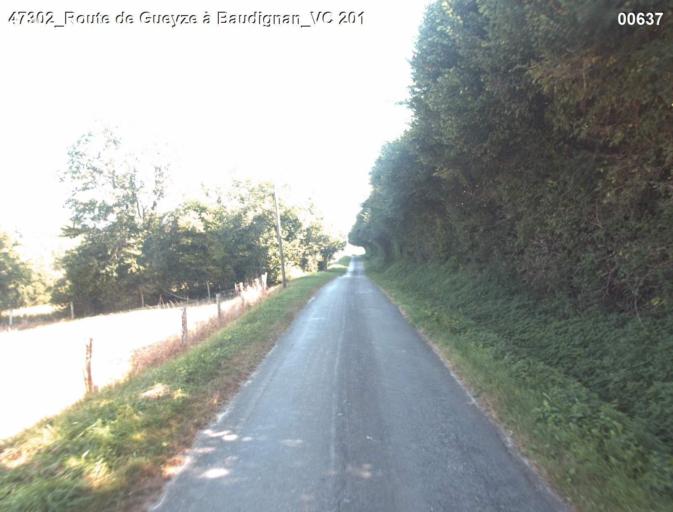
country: FR
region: Midi-Pyrenees
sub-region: Departement du Gers
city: Montreal
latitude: 44.0487
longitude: 0.1262
